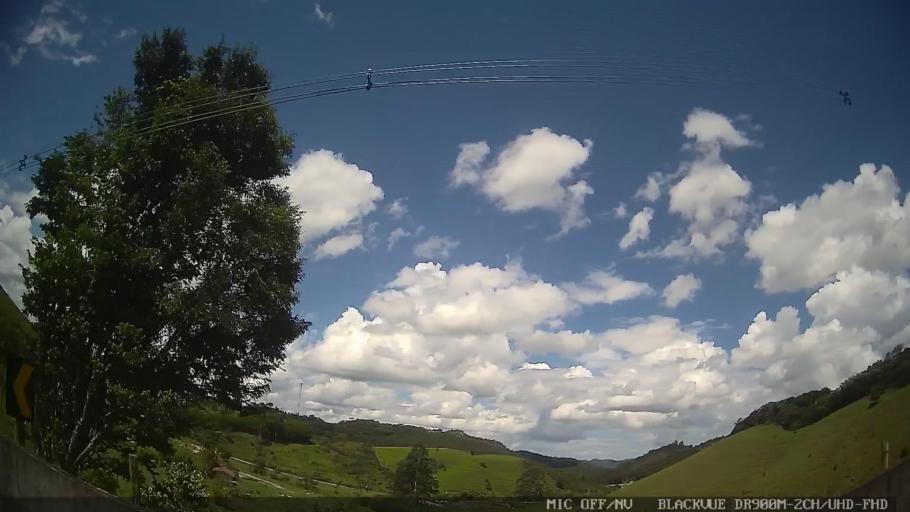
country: BR
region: Sao Paulo
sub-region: Caraguatatuba
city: Caraguatatuba
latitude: -23.5209
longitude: -45.5468
